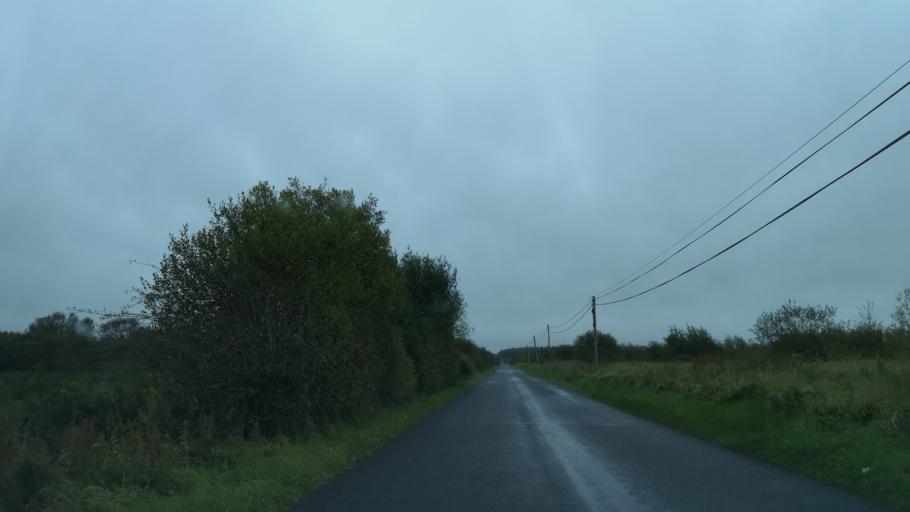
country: IE
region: Connaught
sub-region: Roscommon
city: Ballaghaderreen
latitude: 53.8934
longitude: -8.5742
